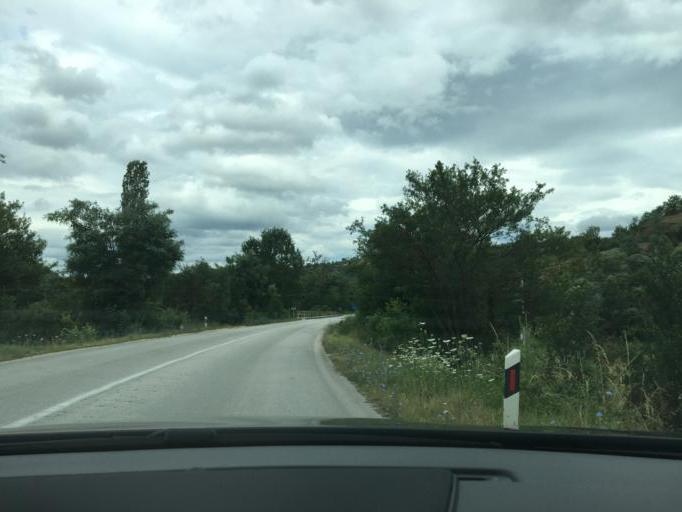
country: MK
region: Kriva Palanka
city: Kriva Palanka
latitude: 42.1762
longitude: 22.2474
